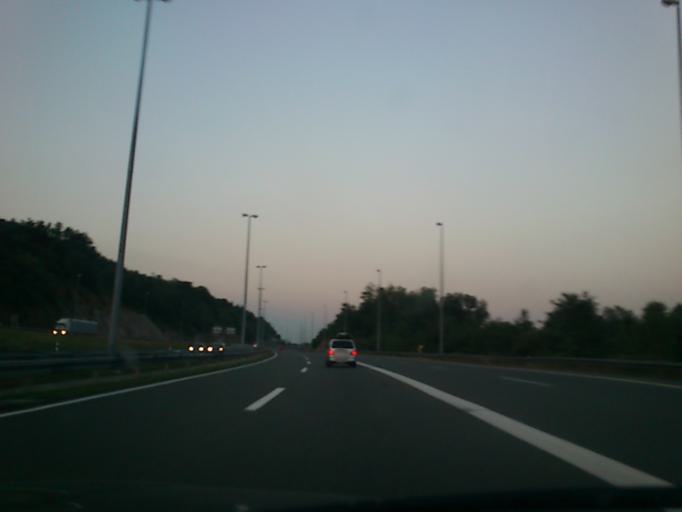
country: HR
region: Karlovacka
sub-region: Grad Ogulin
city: Ogulin
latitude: 45.4077
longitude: 15.2603
